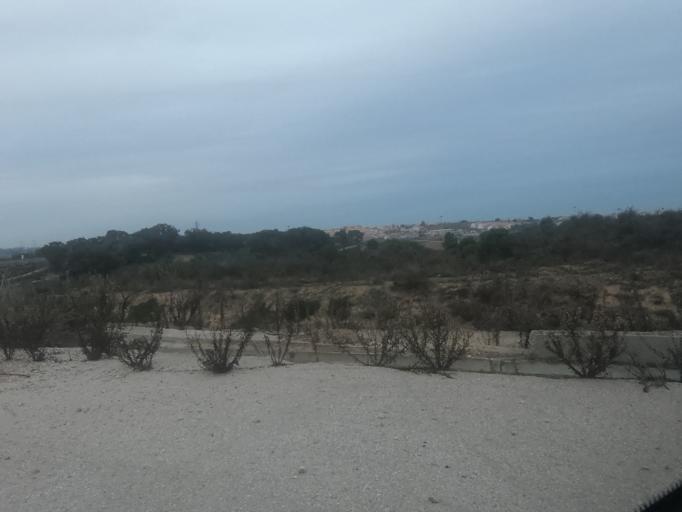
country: PT
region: Setubal
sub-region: Setubal
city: Setubal
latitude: 38.5070
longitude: -8.8374
